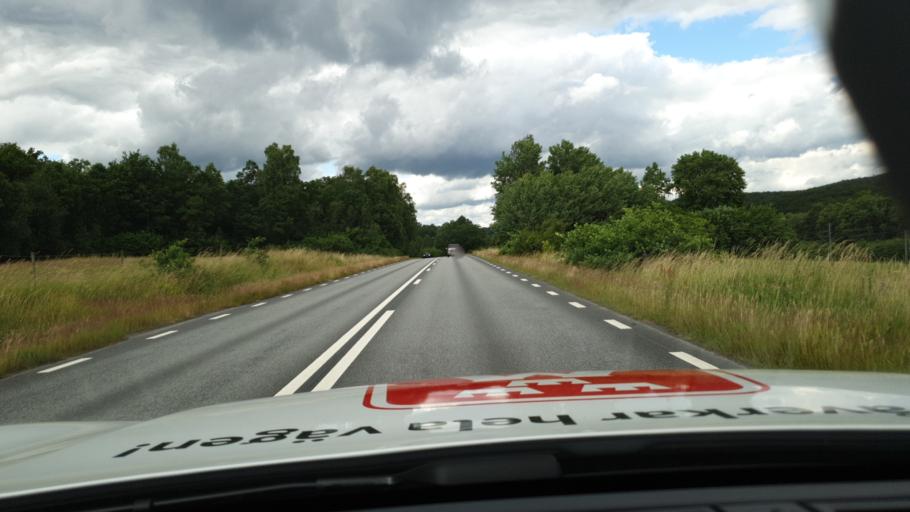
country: SE
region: Skane
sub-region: Hassleholms Kommun
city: Tormestorp
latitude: 56.0951
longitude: 13.7376
